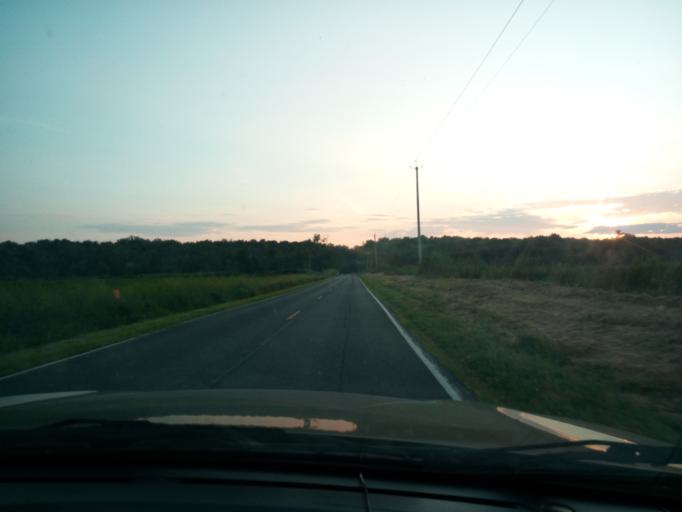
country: US
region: New York
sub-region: Wayne County
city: Clyde
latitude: 43.0214
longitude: -76.7897
